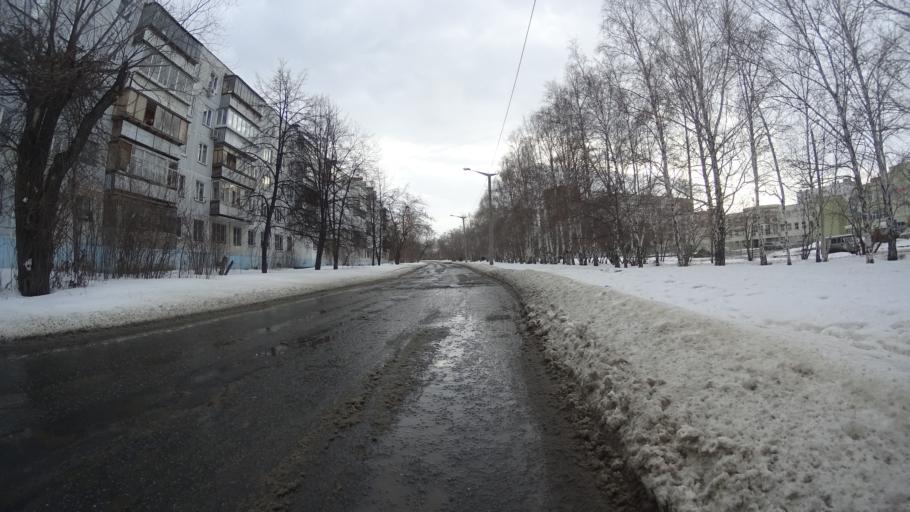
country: RU
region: Chelyabinsk
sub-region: Gorod Chelyabinsk
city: Chelyabinsk
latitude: 55.1989
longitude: 61.3228
